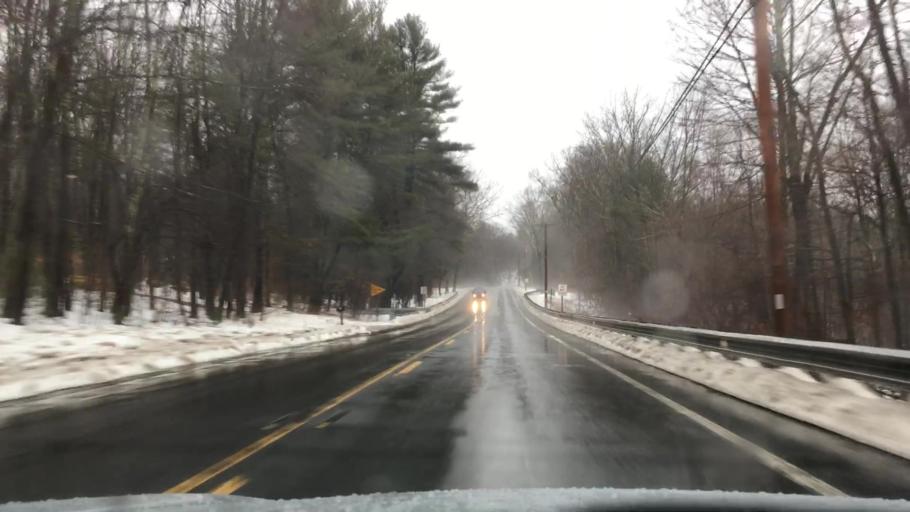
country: US
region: Massachusetts
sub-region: Hampshire County
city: Belchertown
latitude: 42.3177
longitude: -72.4063
